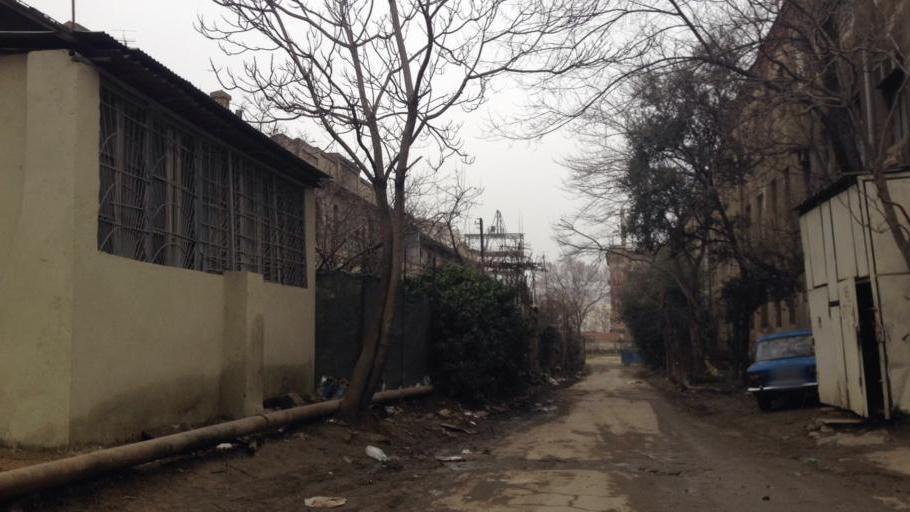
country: AZ
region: Baki
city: Baku
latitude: 40.3874
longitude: 49.8755
